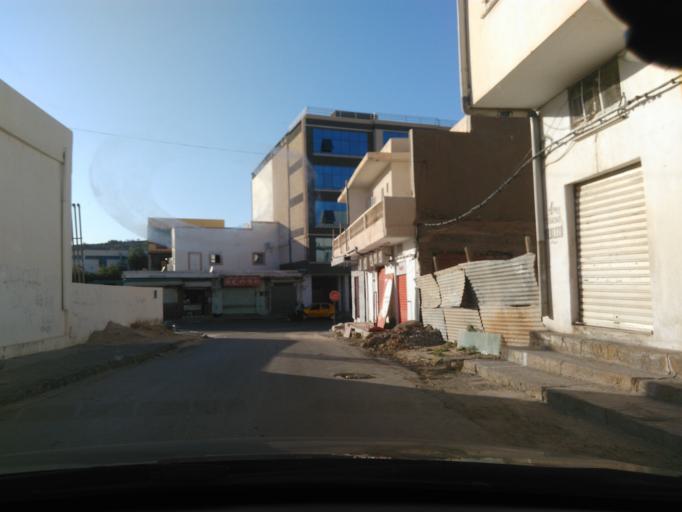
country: TN
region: Tataouine
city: Tataouine
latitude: 32.9282
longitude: 10.4461
